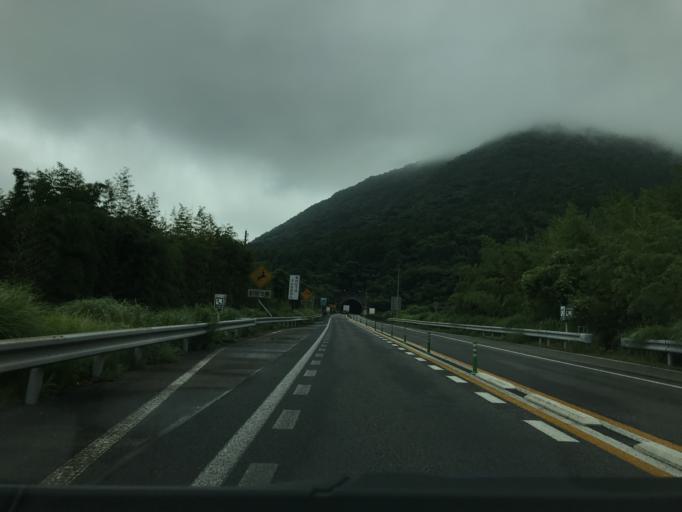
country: JP
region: Oita
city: Bungo-Takada-shi
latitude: 33.4906
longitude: 131.3228
